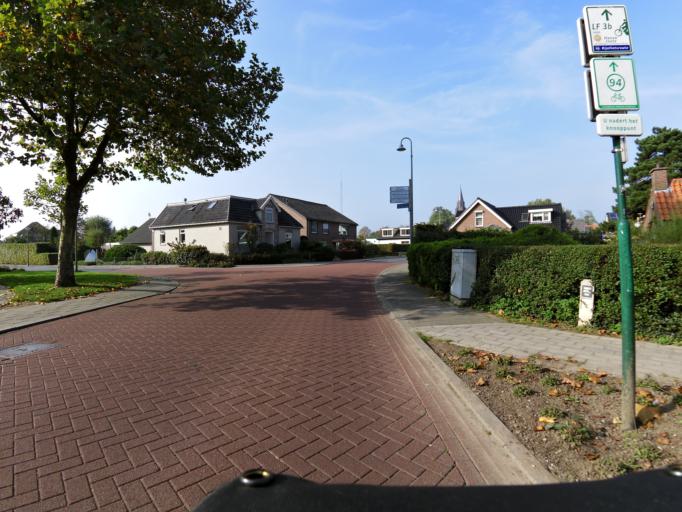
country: NL
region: Gelderland
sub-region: Gemeente Zevenaar
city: Zevenaar
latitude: 51.8611
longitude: 6.0496
